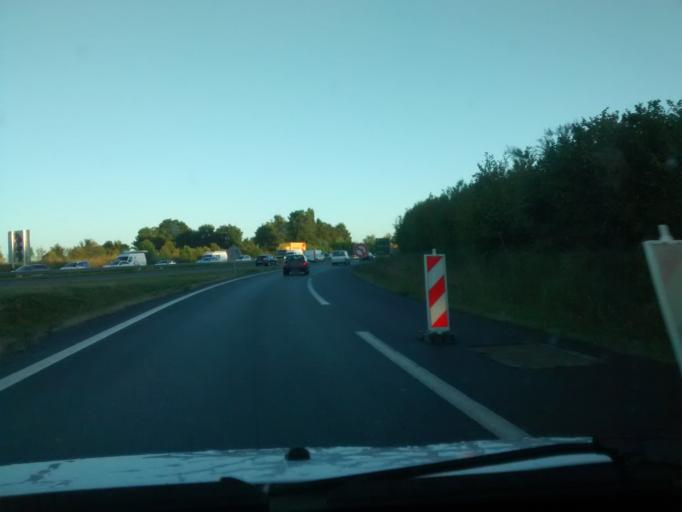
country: FR
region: Brittany
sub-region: Departement d'Ille-et-Vilaine
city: Saint-Gregoire
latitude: 48.1448
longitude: -1.6979
